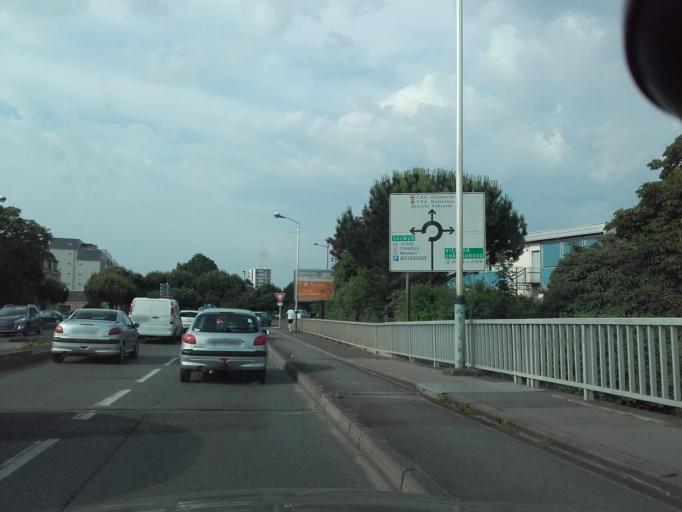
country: FR
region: Centre
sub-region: Departement d'Indre-et-Loire
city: Tours
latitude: 47.3729
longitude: 0.6784
